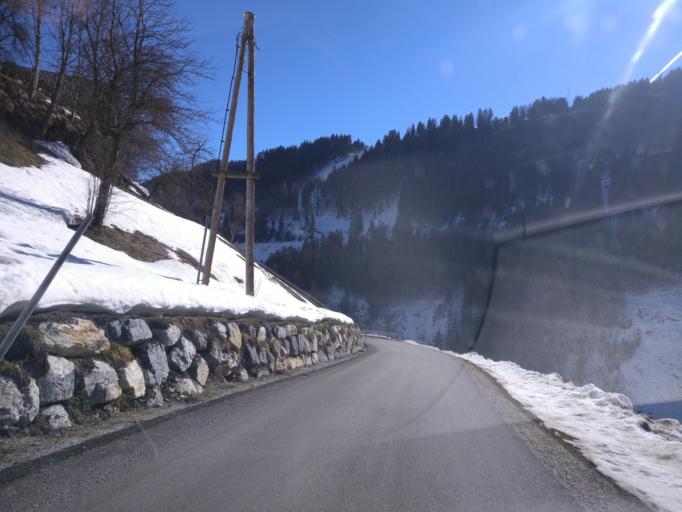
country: AT
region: Salzburg
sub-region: Politischer Bezirk Sankt Johann im Pongau
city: Sankt Johann im Pongau
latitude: 47.3321
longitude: 13.2323
